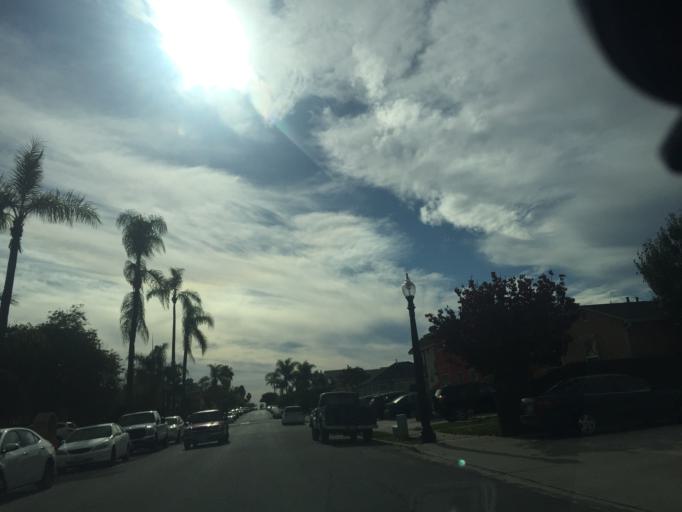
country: US
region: California
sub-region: San Diego County
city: Lemon Grove
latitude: 32.7598
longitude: -117.0857
